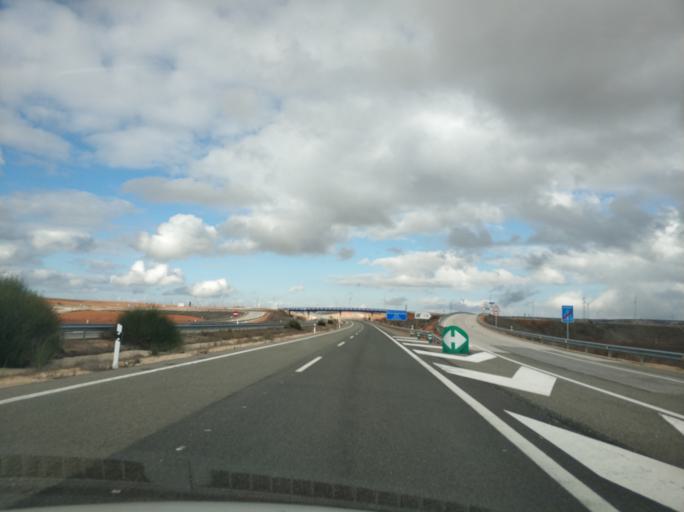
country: ES
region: Castille and Leon
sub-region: Provincia de Soria
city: Alcubilla de las Penas
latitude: 41.2581
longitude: -2.4733
